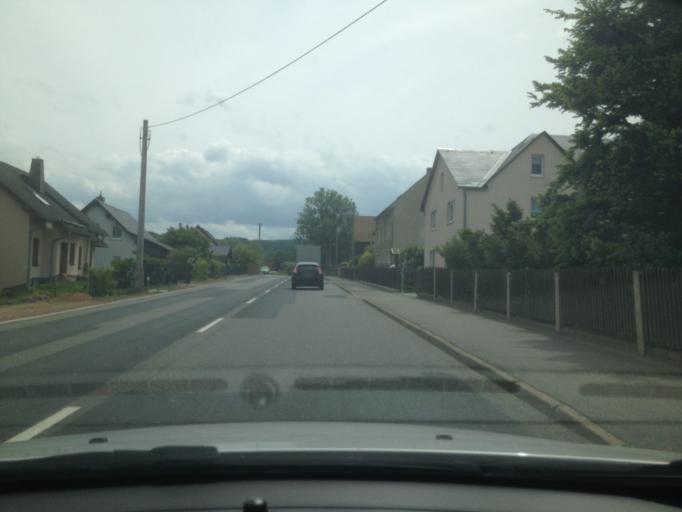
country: DE
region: Saxony
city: Stollberg
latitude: 50.6806
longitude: 12.7632
